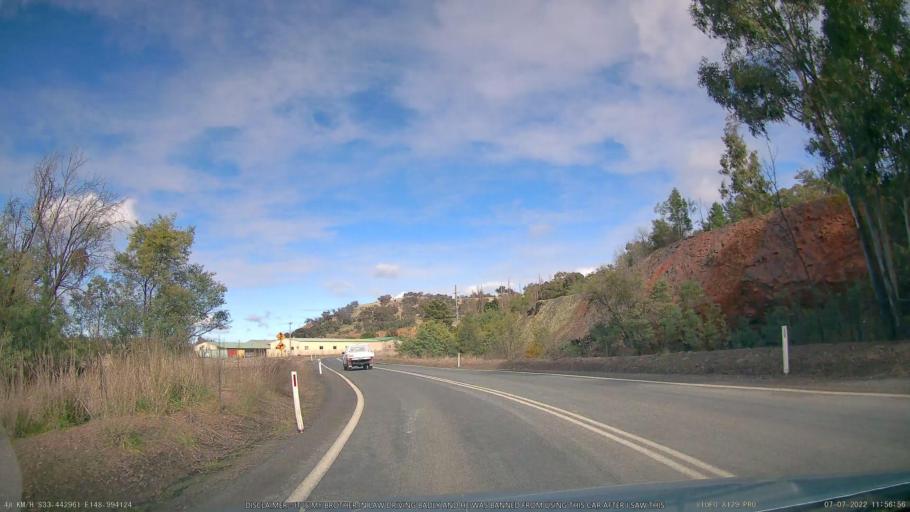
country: AU
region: New South Wales
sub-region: Orange Municipality
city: Orange
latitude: -33.4431
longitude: 148.9933
